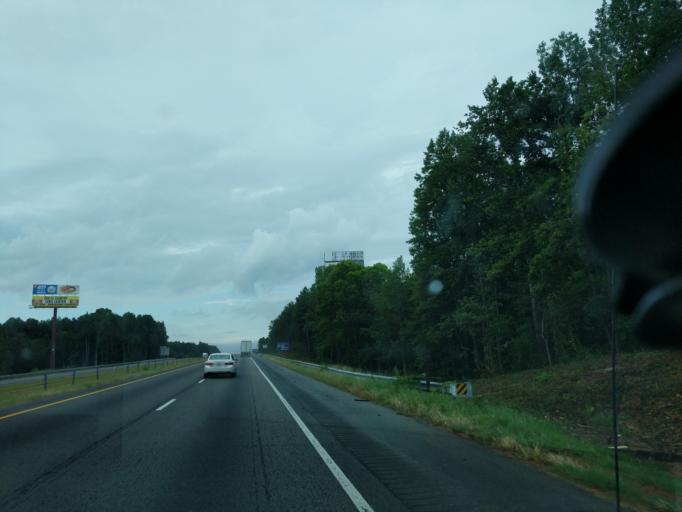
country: US
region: Georgia
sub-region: Jackson County
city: Commerce
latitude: 34.2367
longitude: -83.4898
